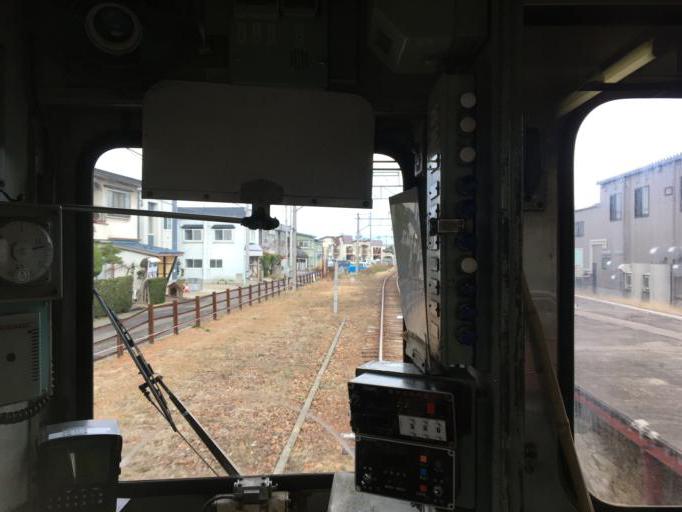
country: JP
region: Aomori
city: Hirosaki
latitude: 40.5832
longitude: 140.4706
